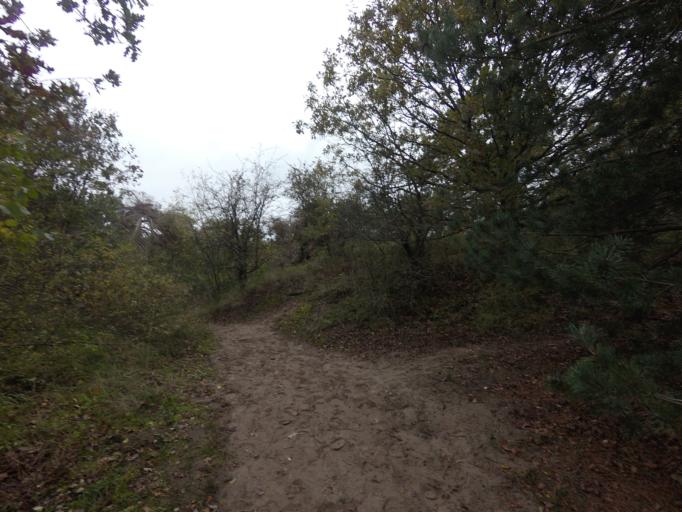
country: NL
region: South Holland
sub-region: Gemeente Wassenaar
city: Wassenaar
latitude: 52.1325
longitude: 4.3523
